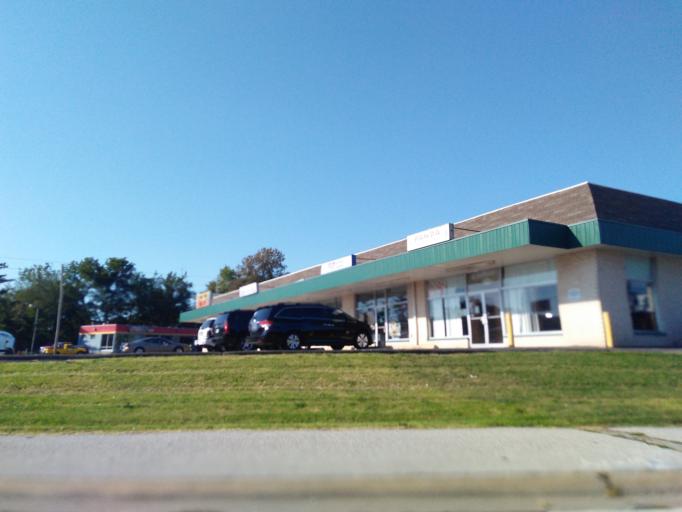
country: US
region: Missouri
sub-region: Saint Louis County
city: Concord
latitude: 38.5204
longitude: -90.3616
